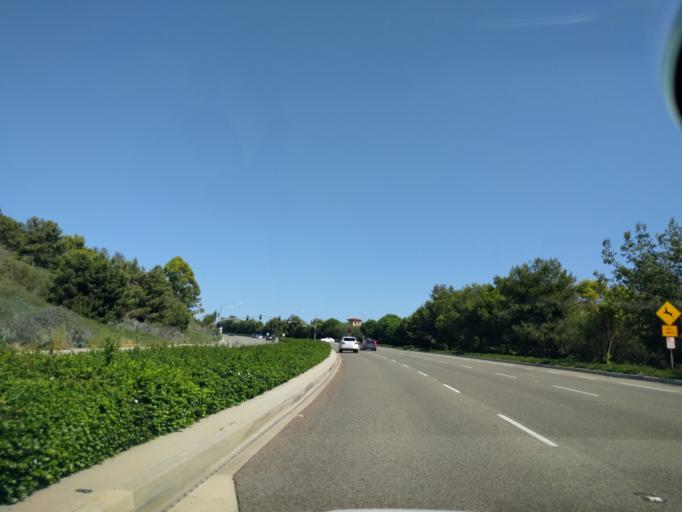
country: US
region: California
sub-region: Orange County
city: San Joaquin Hills
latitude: 33.5836
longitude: -117.8405
